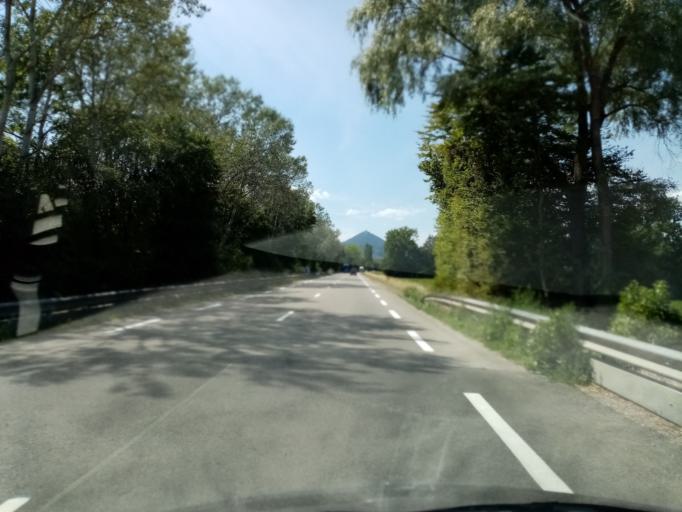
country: FR
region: Alsace
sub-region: Departement du Bas-Rhin
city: Selestat
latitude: 48.2477
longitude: 7.4491
